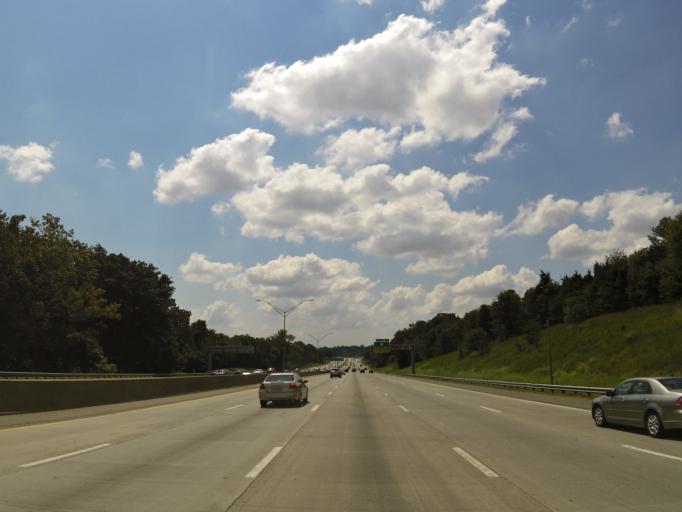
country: US
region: North Carolina
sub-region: Cabarrus County
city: Harrisburg
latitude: 35.3232
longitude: -80.7491
